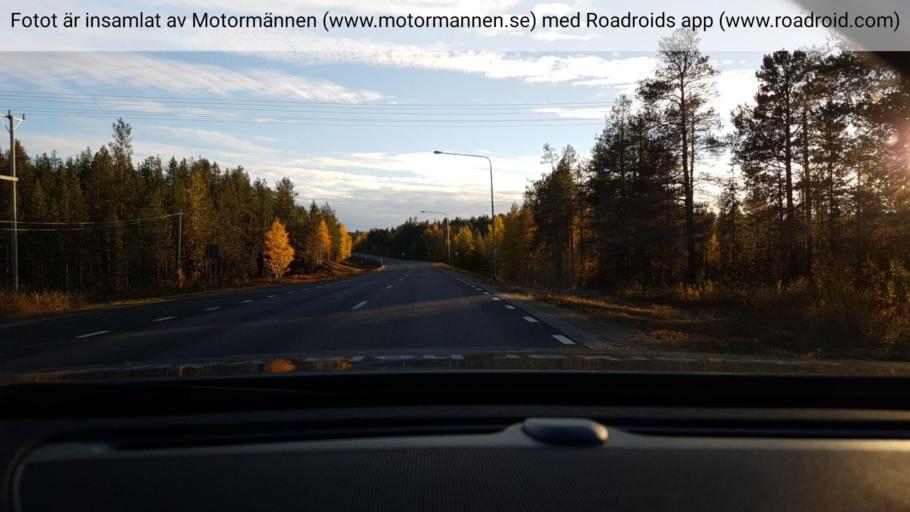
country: SE
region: Norrbotten
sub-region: Jokkmokks Kommun
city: Jokkmokk
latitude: 66.6020
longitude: 19.8176
